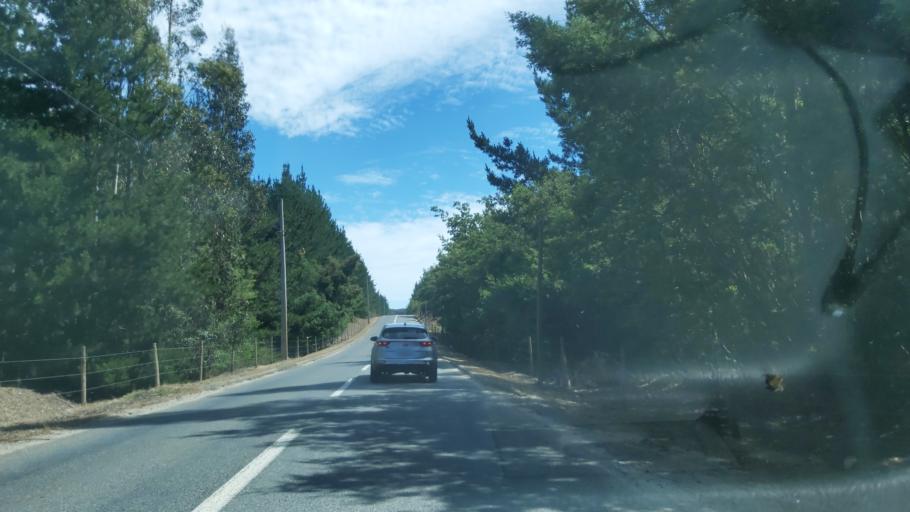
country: CL
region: Maule
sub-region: Provincia de Talca
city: Constitucion
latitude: -35.5273
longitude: -72.5395
